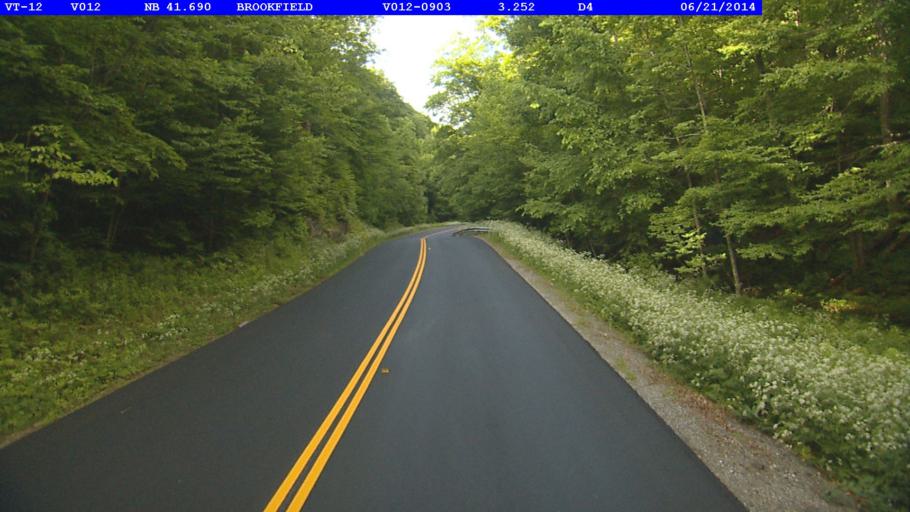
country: US
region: Vermont
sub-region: Washington County
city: Northfield
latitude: 44.0492
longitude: -72.6437
